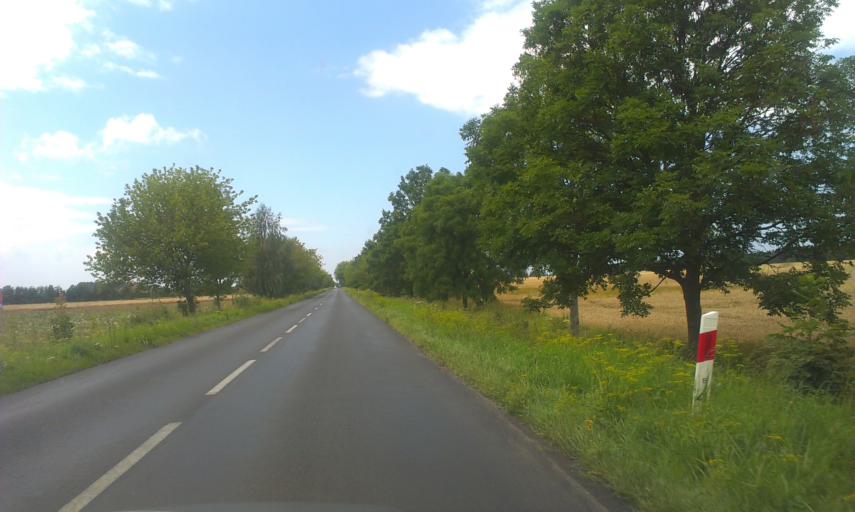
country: PL
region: West Pomeranian Voivodeship
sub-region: Powiat kolobrzeski
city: Dygowo
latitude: 54.1431
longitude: 15.6900
